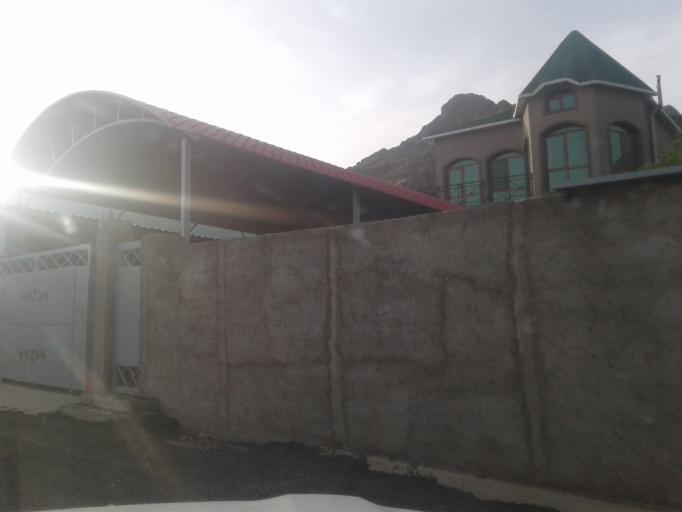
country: TM
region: Balkan
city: Turkmenbasy
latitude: 40.0074
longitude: 52.9653
